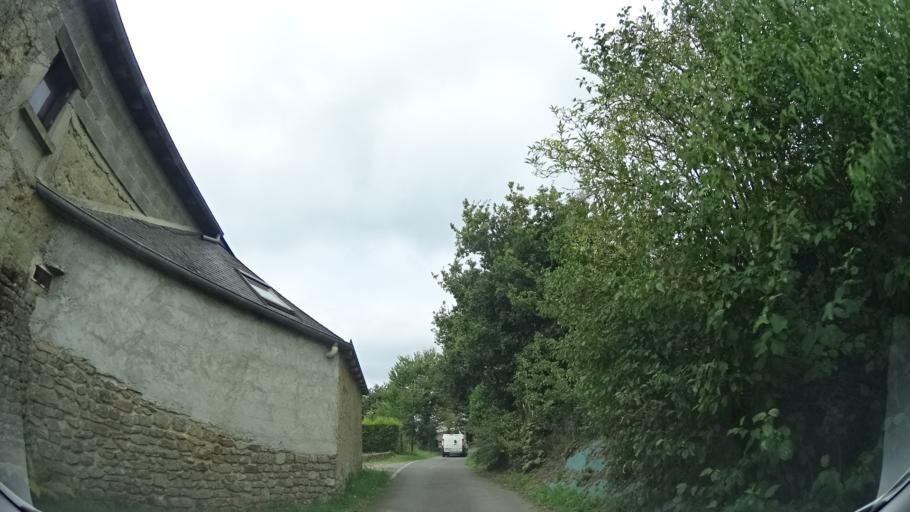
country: FR
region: Brittany
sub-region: Departement d'Ille-et-Vilaine
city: Romille
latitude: 48.2839
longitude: -1.8902
